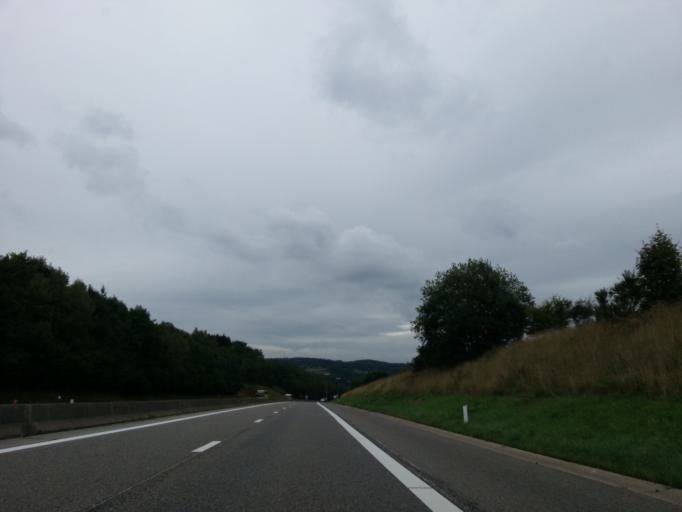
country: BE
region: Wallonia
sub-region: Province de Liege
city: Malmedy
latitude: 50.3618
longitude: 6.0384
